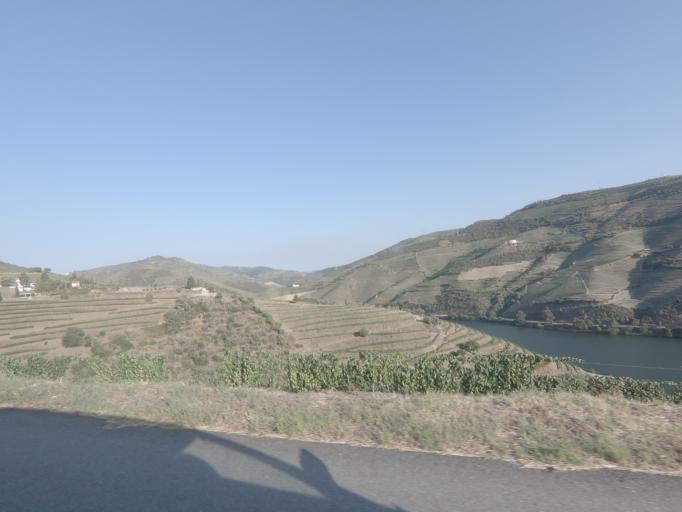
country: PT
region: Viseu
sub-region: Tabuaco
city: Tabuaco
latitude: 41.1623
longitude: -7.6003
